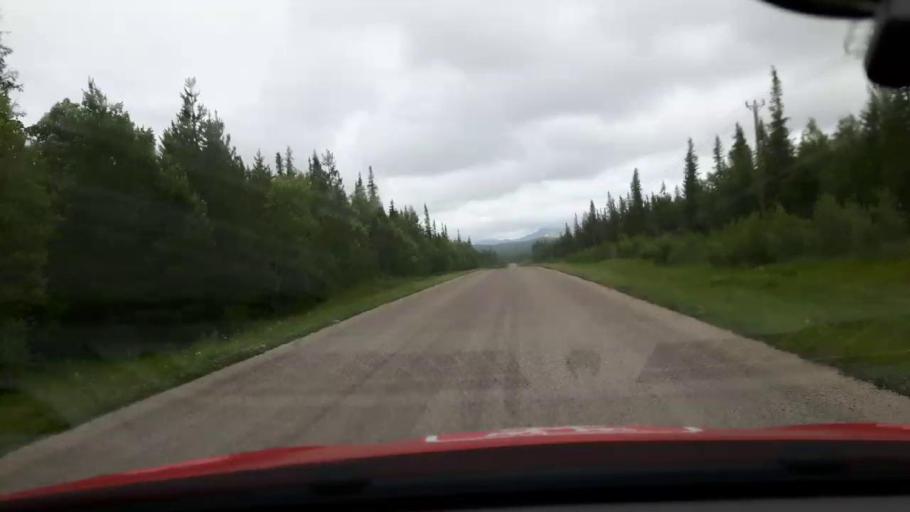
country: NO
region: Nord-Trondelag
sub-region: Meraker
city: Meraker
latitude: 63.2772
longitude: 12.3577
